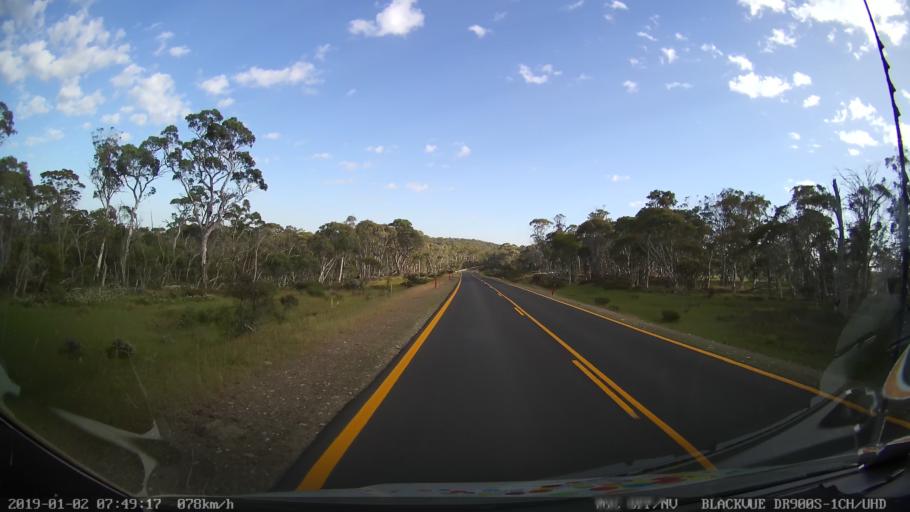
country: AU
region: New South Wales
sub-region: Tumut Shire
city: Tumut
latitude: -35.7436
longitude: 148.5220
